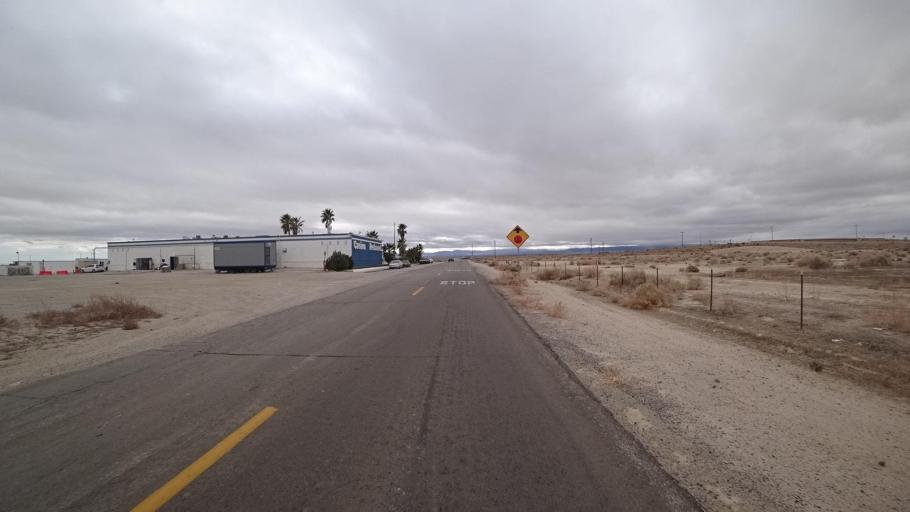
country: US
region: California
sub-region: Kern County
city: Rosamond
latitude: 34.8232
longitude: -118.1667
